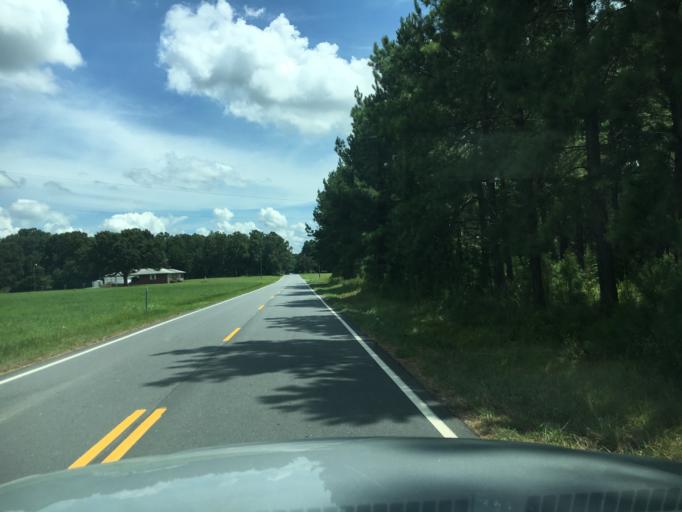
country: US
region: South Carolina
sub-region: Anderson County
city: Belton
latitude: 34.5321
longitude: -82.4340
